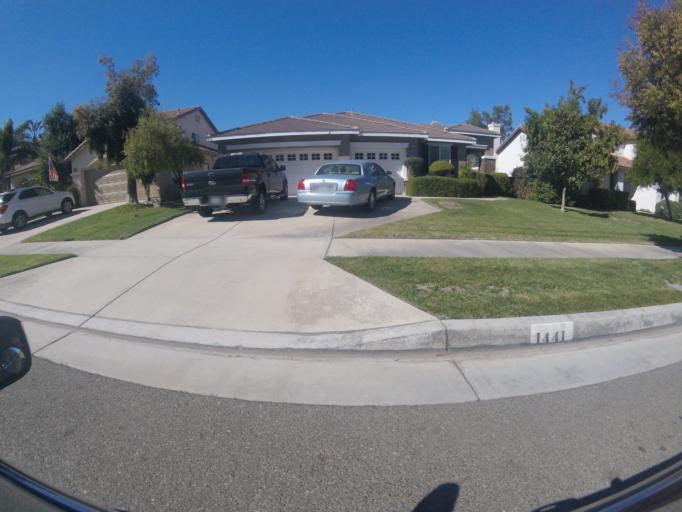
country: US
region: California
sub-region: San Bernardino County
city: Mentone
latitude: 34.0736
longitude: -117.1442
